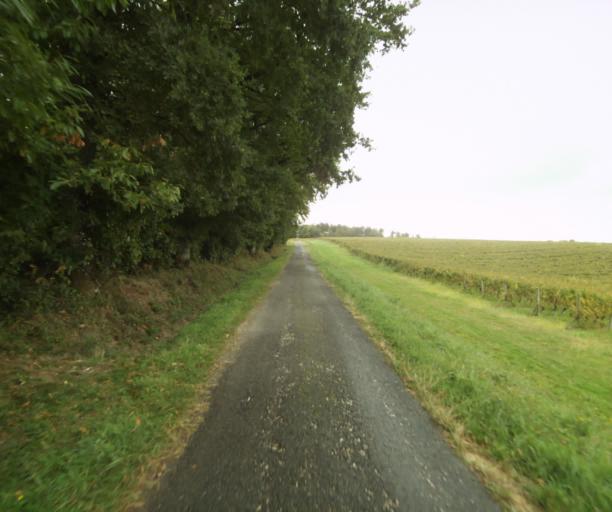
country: FR
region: Midi-Pyrenees
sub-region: Departement du Gers
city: Eauze
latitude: 43.8804
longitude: 0.0705
